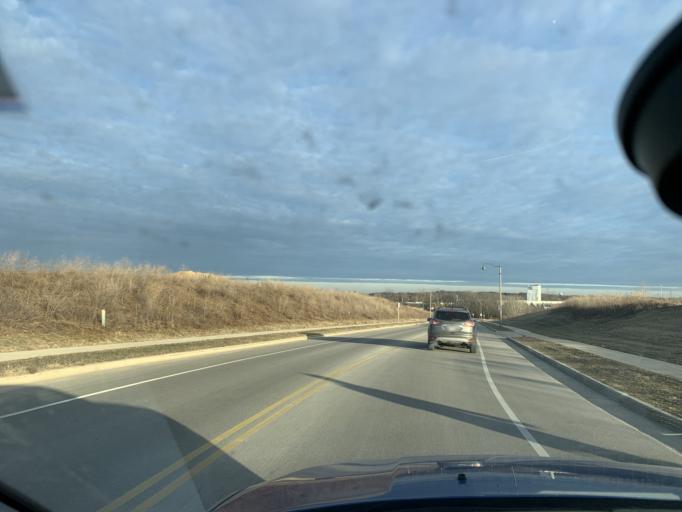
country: US
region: Wisconsin
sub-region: Dane County
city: Fitchburg
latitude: 43.0187
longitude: -89.4798
